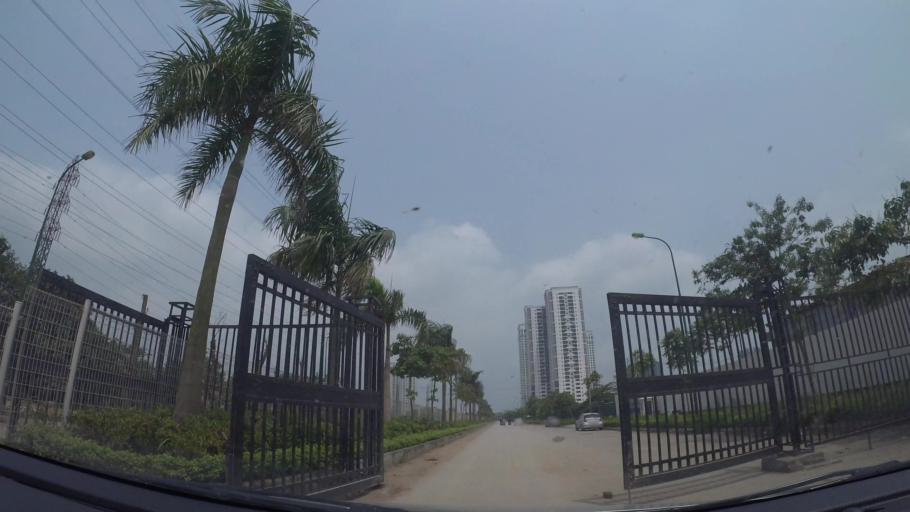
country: VN
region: Ha Noi
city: Tay Ho
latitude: 21.0848
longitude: 105.8068
